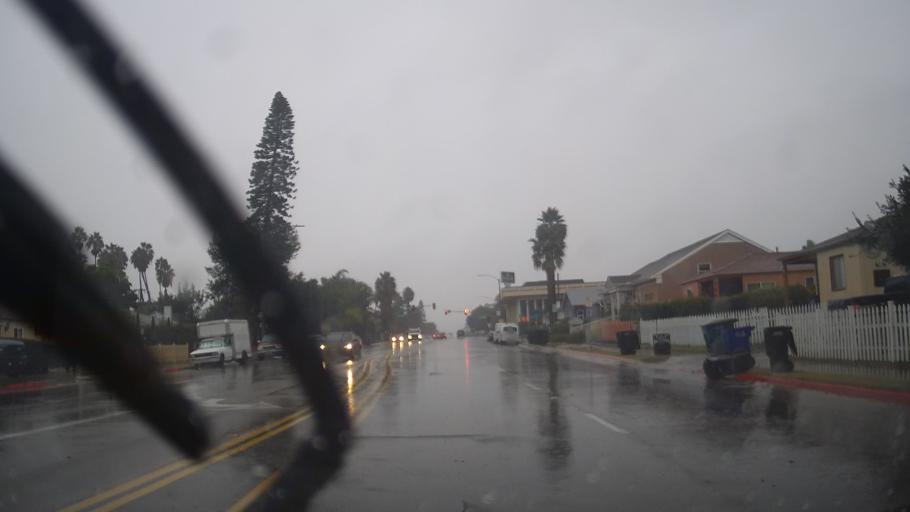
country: US
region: California
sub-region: San Diego County
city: Chula Vista
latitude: 32.6417
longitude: -117.0843
